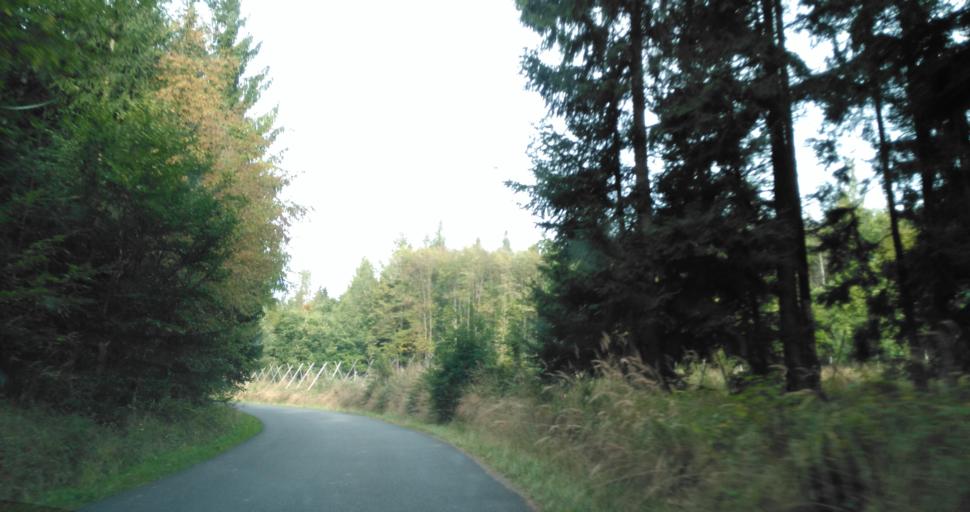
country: CZ
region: Plzensky
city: Zbiroh
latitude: 49.9261
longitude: 13.7988
